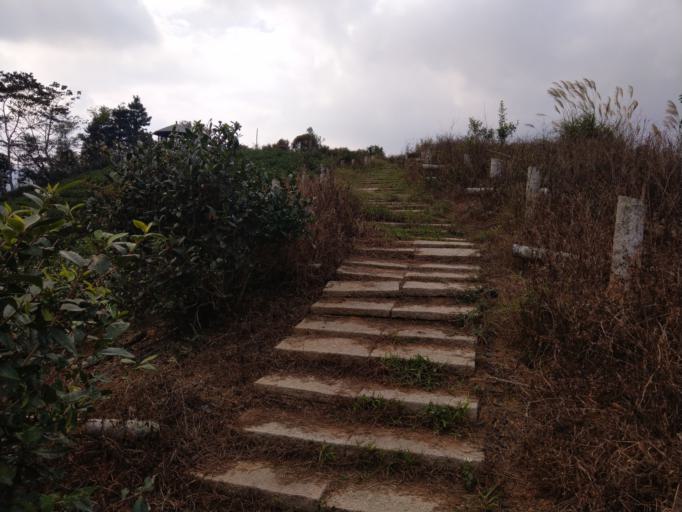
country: TW
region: Taiwan
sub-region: Nantou
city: Puli
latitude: 23.9239
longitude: 120.9157
